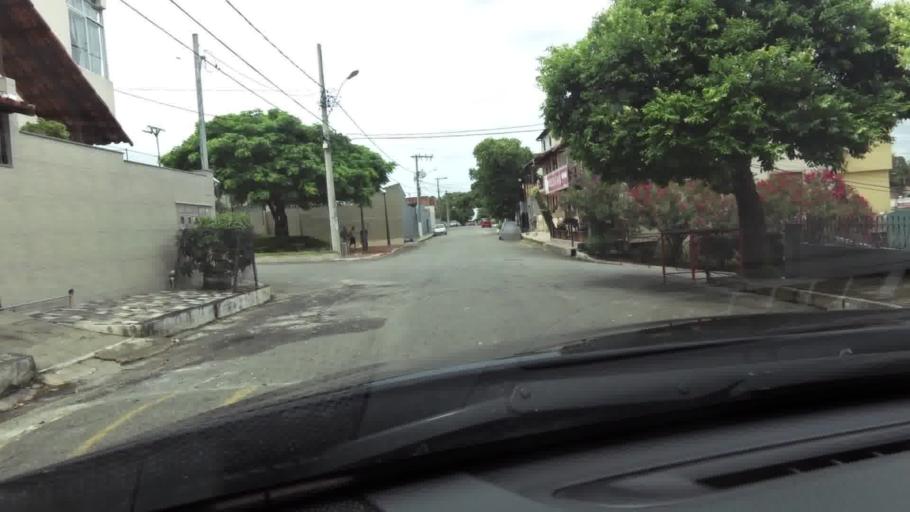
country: BR
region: Espirito Santo
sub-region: Guarapari
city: Guarapari
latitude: -20.6562
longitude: -40.4982
